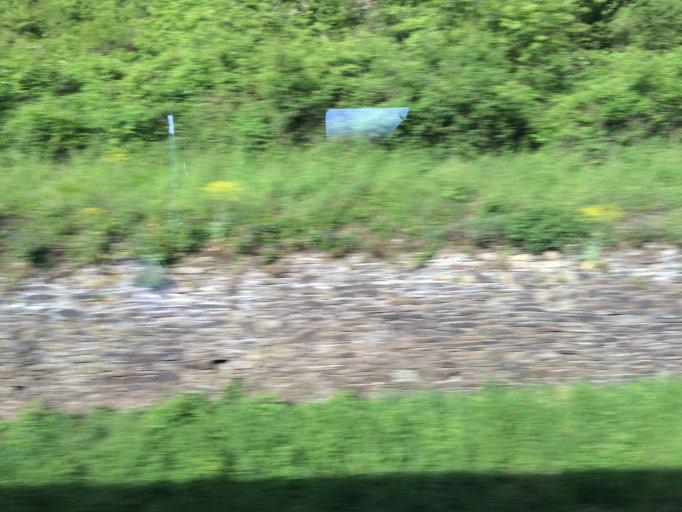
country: DE
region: Rheinland-Pfalz
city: Dorscheid
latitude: 50.0979
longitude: 7.7494
